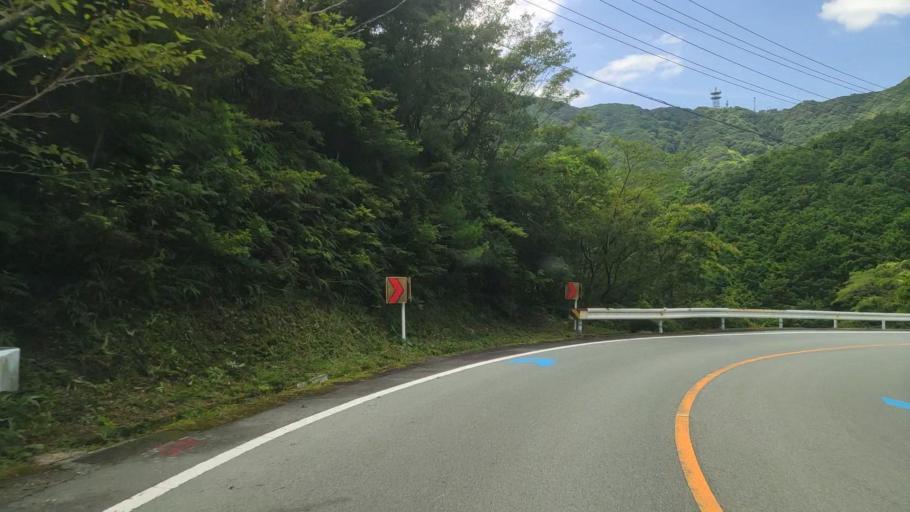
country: JP
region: Mie
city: Owase
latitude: 34.2179
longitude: 136.3828
